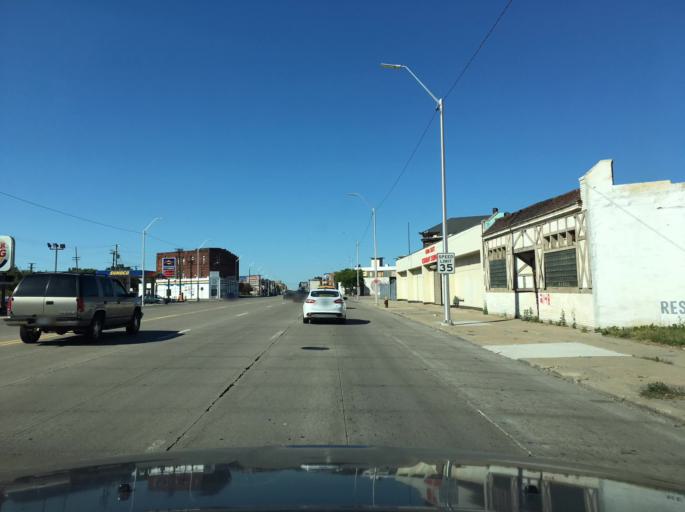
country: US
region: Michigan
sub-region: Wayne County
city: Detroit
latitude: 42.3496
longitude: -83.0340
